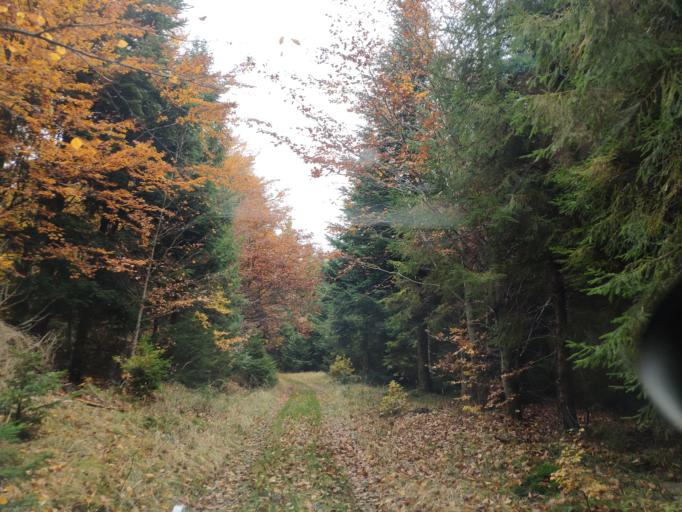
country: SK
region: Kosicky
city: Medzev
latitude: 48.7485
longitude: 20.9852
